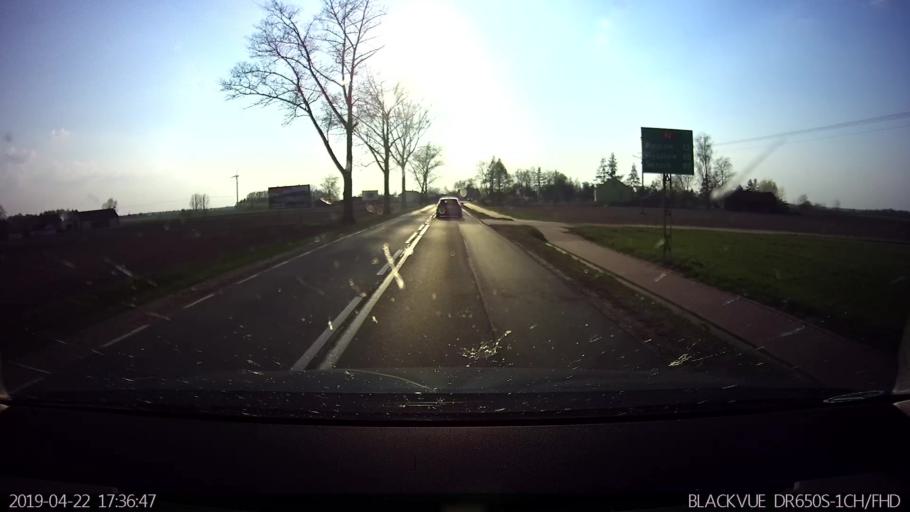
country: PL
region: Masovian Voivodeship
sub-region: Powiat sokolowski
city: Sokolow Podlaski
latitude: 52.4075
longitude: 22.1842
